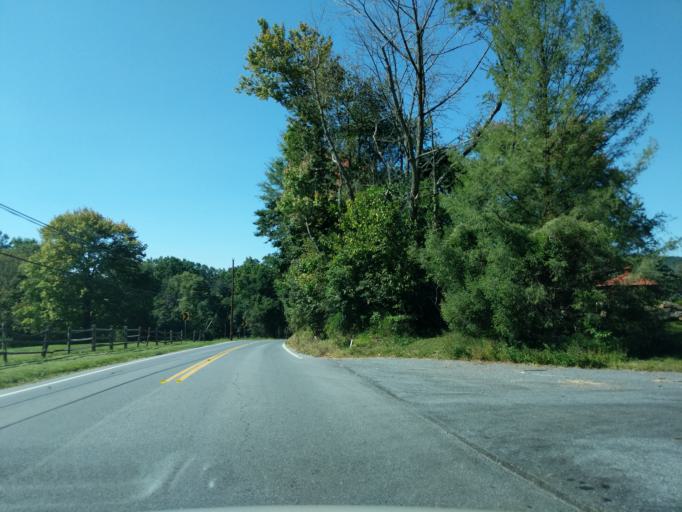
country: US
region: Pennsylvania
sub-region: Montgomery County
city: East Greenville
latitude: 40.4500
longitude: -75.4920
